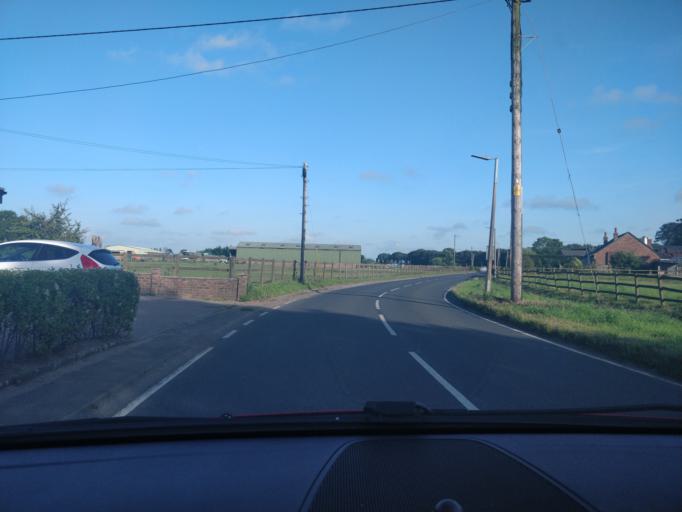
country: GB
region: England
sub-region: Lancashire
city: Banks
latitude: 53.6518
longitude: -2.8762
